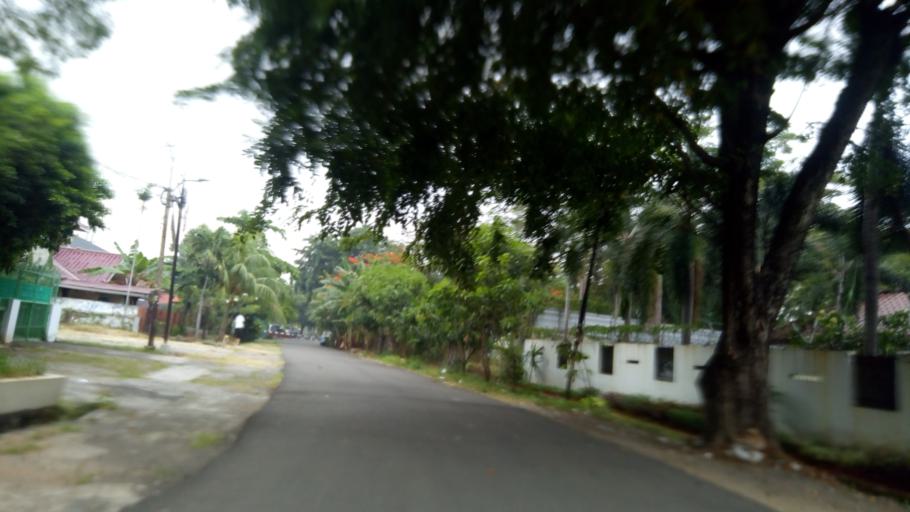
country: ID
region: Jakarta Raya
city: Jakarta
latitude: -6.1521
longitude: 106.8407
